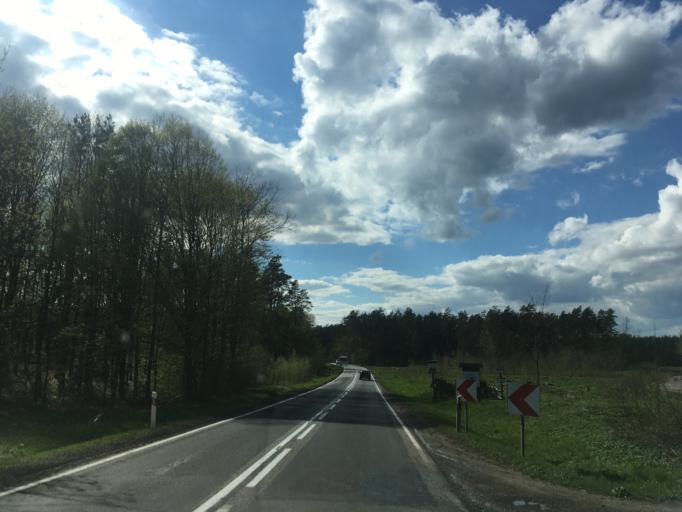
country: PL
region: Warmian-Masurian Voivodeship
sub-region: Powiat szczycienski
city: Szczytno
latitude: 53.5712
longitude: 20.9463
